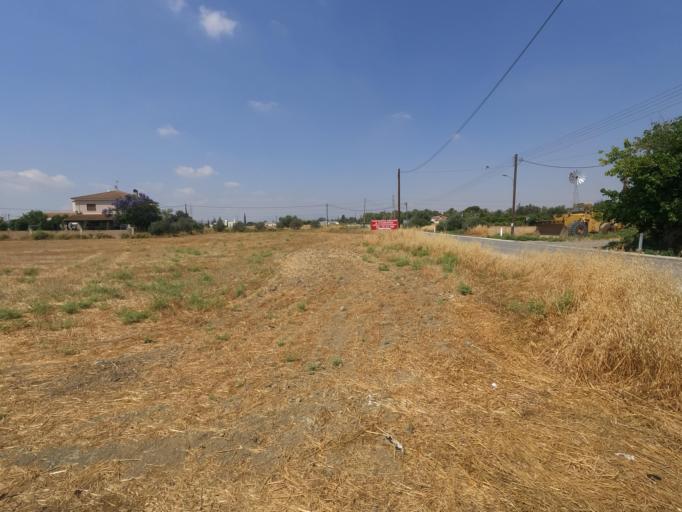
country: CY
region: Lefkosia
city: Dali
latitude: 35.0391
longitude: 33.4393
